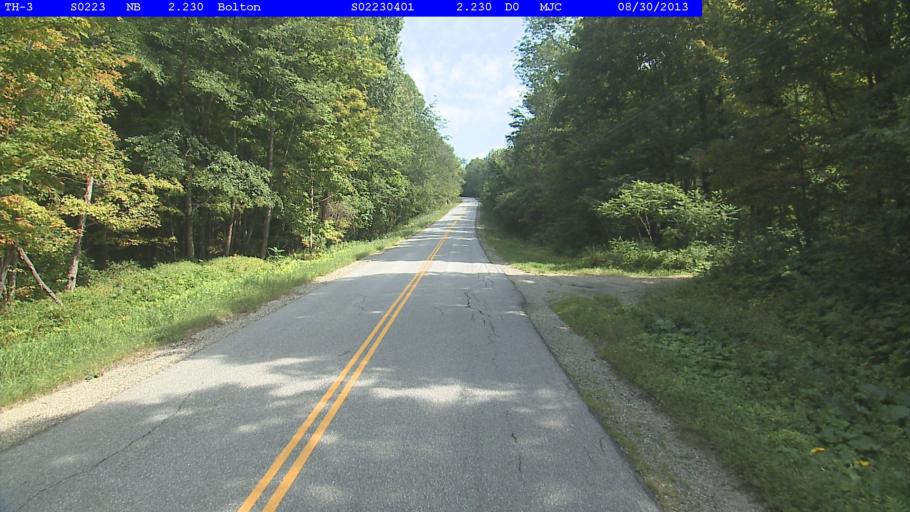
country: US
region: Vermont
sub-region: Washington County
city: Waterbury
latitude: 44.4013
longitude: -72.8773
